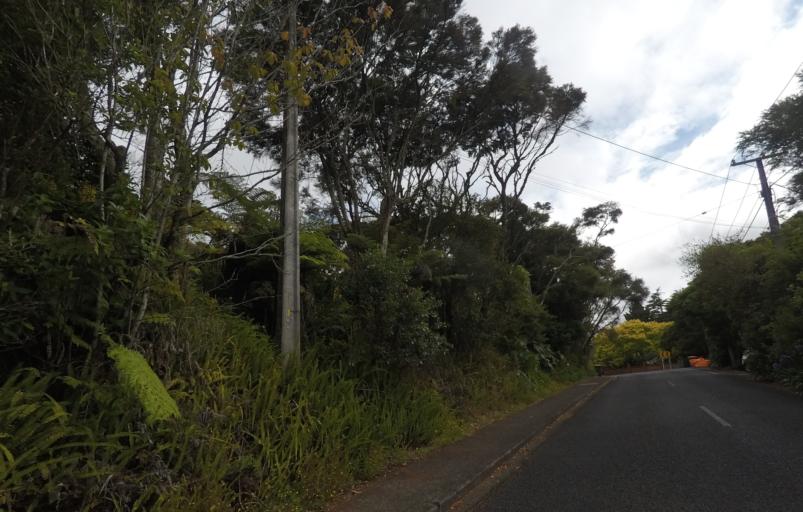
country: NZ
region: Auckland
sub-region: Auckland
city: Titirangi
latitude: -36.9384
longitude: 174.6689
